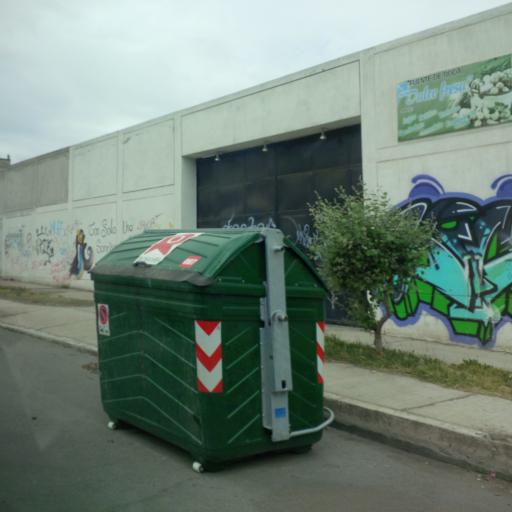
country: EC
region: Chimborazo
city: Riobamba
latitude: -1.6538
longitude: -78.6733
